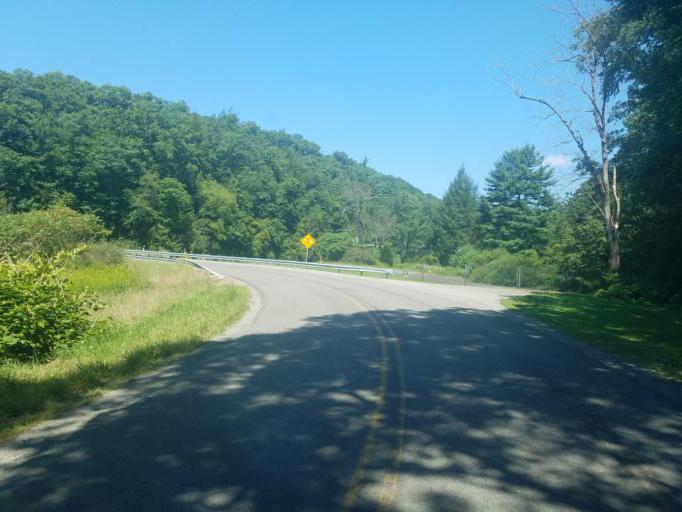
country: US
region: Pennsylvania
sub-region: Clarion County
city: Knox
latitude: 41.1718
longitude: -79.4777
